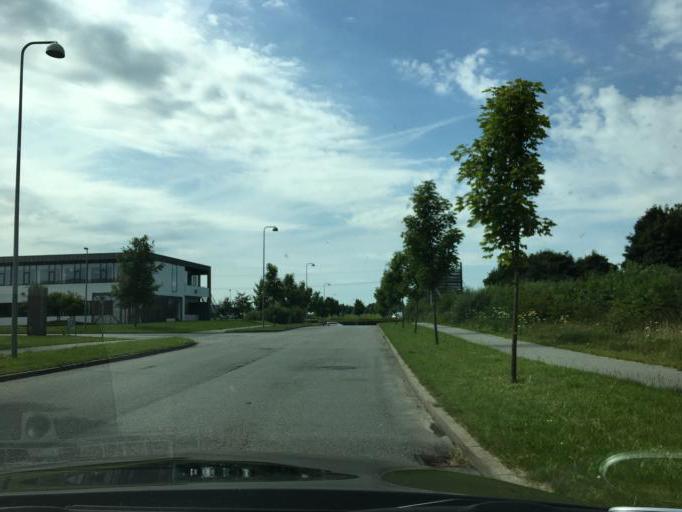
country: DK
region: South Denmark
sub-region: Kolding Kommune
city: Kolding
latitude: 55.5341
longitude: 9.4657
